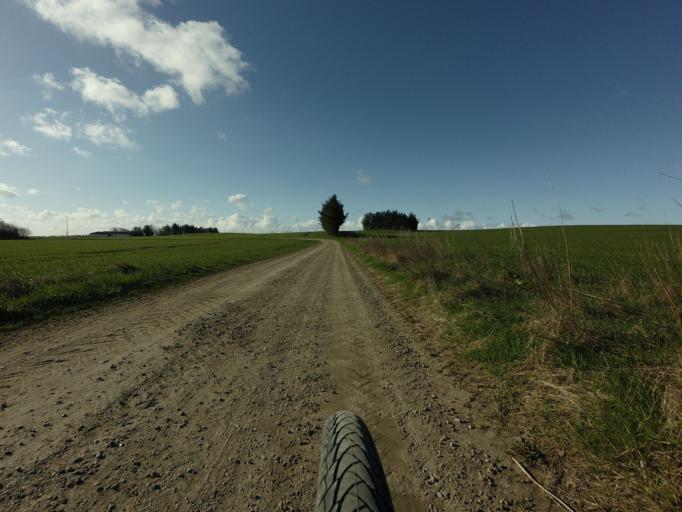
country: DK
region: North Denmark
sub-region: Hjorring Kommune
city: Vra
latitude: 57.3675
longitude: 9.8137
